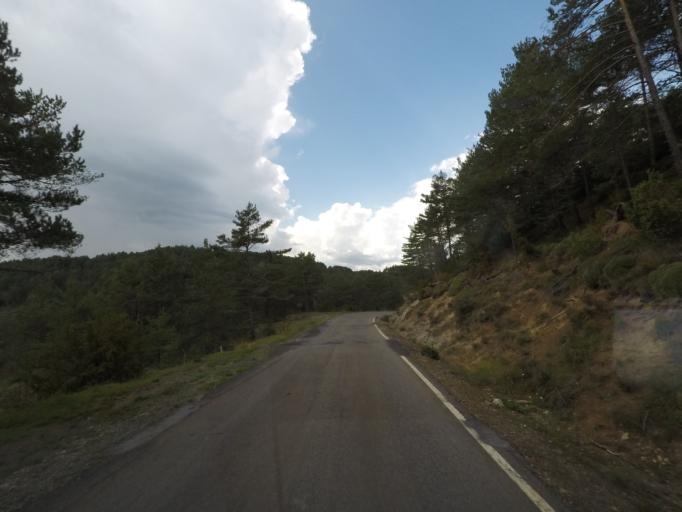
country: ES
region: Aragon
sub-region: Provincia de Huesca
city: Fiscal
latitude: 42.4024
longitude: -0.0735
